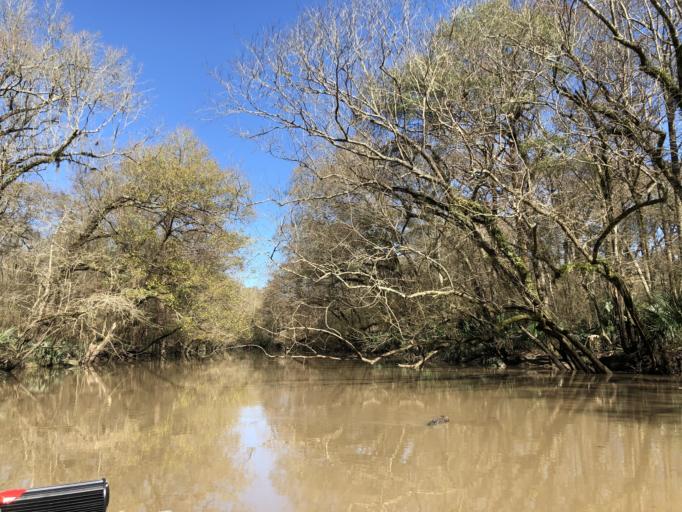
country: US
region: Louisiana
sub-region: Calcasieu Parish
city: Iowa
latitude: 30.3124
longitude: -93.0750
